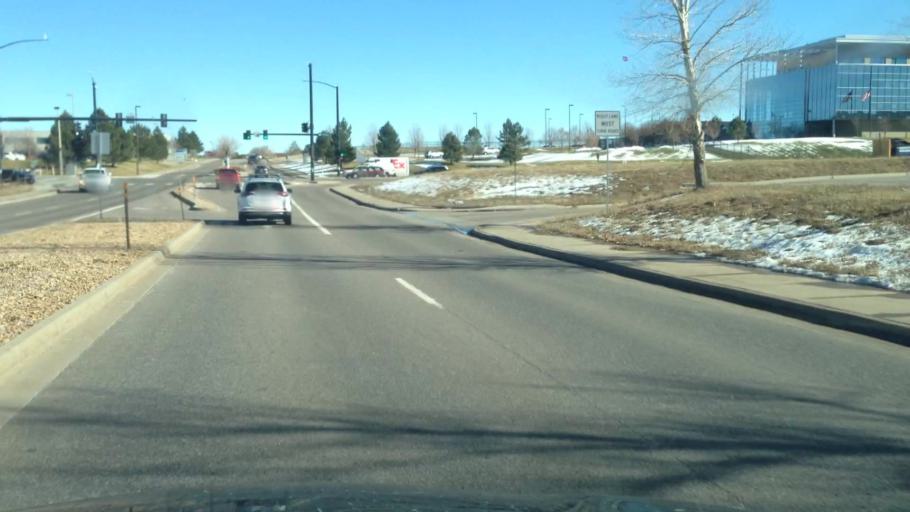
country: US
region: Colorado
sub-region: Arapahoe County
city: Dove Valley
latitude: 39.5881
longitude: -104.8495
